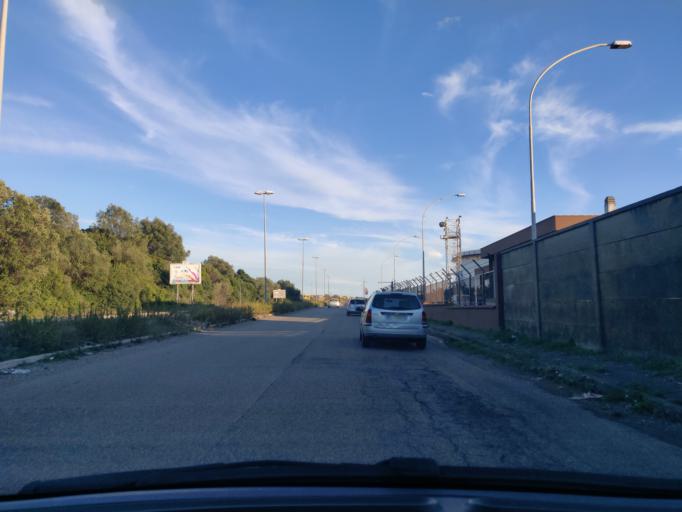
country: IT
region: Latium
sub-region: Citta metropolitana di Roma Capitale
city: Civitavecchia
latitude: 42.1123
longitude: 11.7817
